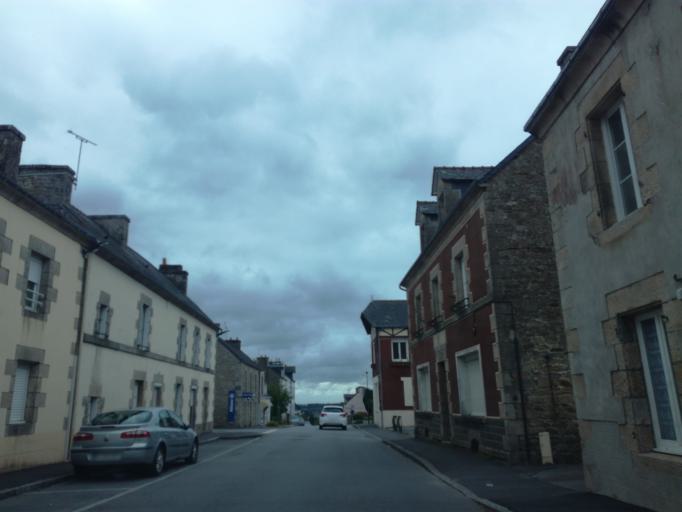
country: FR
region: Brittany
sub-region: Departement du Morbihan
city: Cleguerec
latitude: 48.1235
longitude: -3.0687
